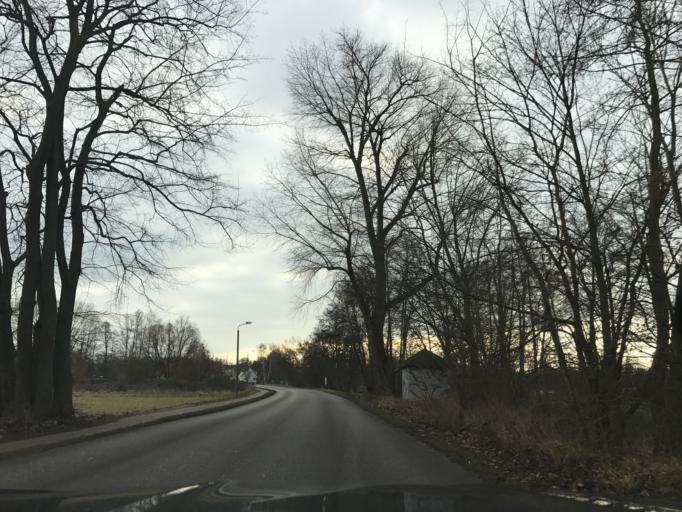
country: DE
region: Brandenburg
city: Brandenburg an der Havel
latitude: 52.3728
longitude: 12.5466
